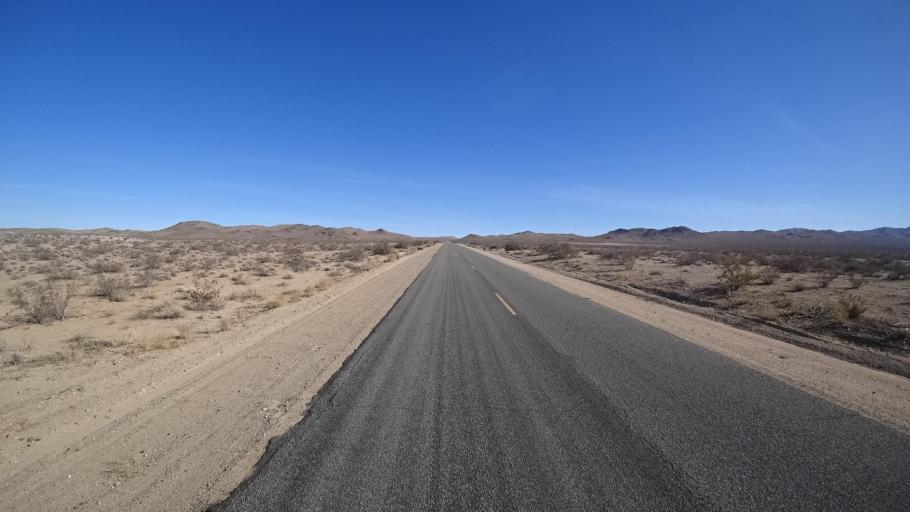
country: US
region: California
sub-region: Kern County
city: Ridgecrest
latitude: 35.5520
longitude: -117.7260
